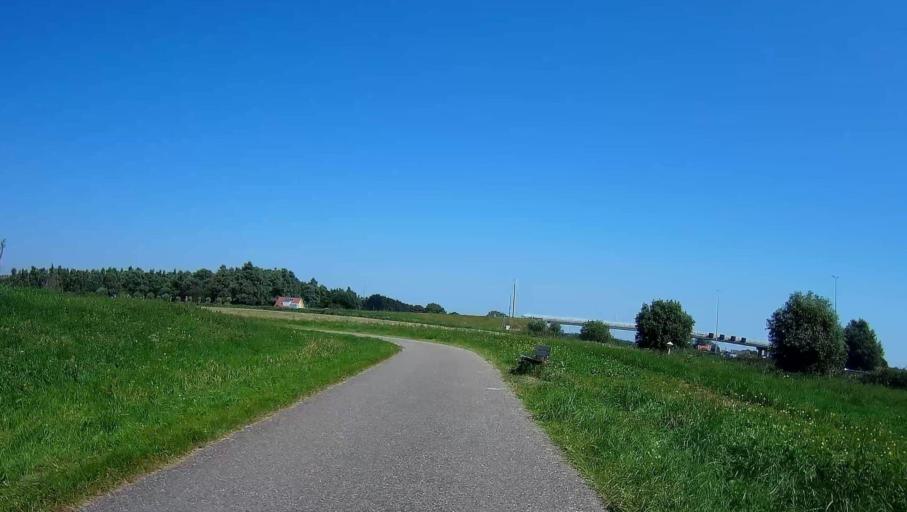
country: NL
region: South Holland
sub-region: Gemeente Voorschoten
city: Voorschoten
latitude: 52.0991
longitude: 4.4395
